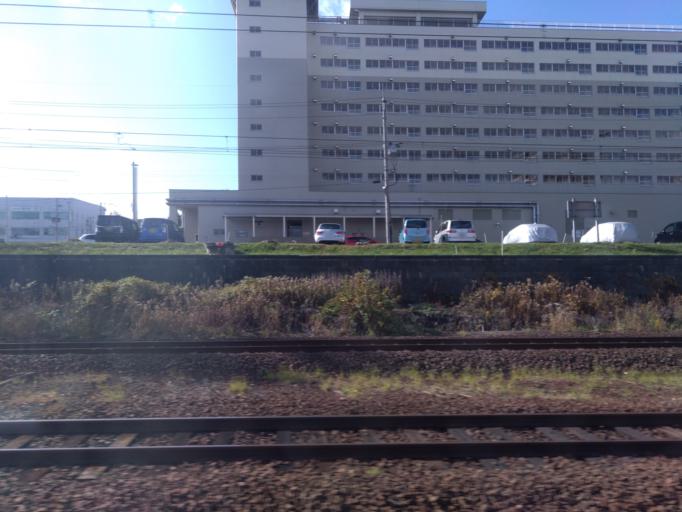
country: JP
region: Hokkaido
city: Kitahiroshima
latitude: 42.9769
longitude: 141.5635
